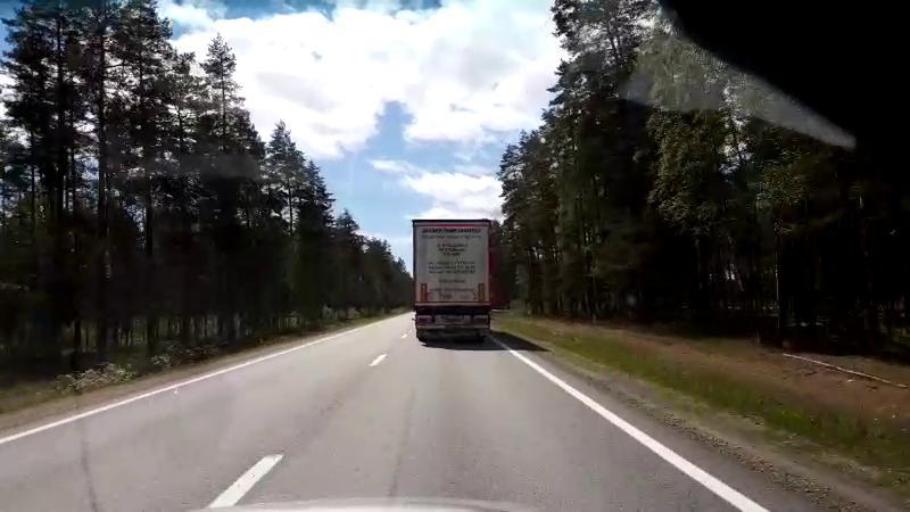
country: LV
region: Salacgrivas
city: Salacgriva
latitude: 57.5477
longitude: 24.4326
